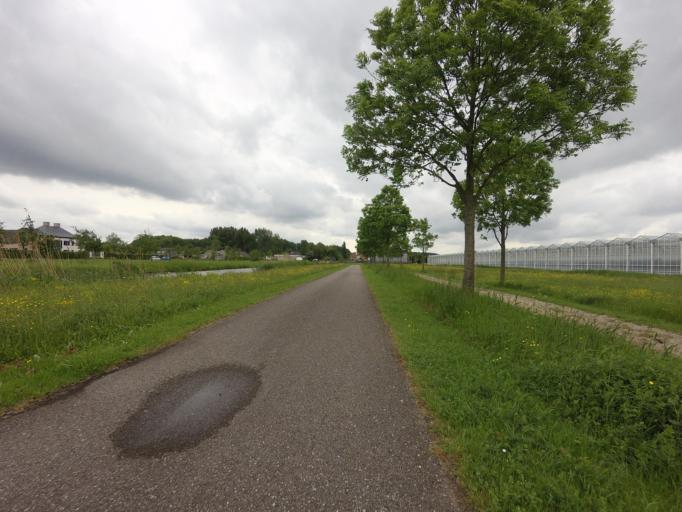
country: NL
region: South Holland
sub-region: Gemeente Lansingerland
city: Bergschenhoek
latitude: 51.9786
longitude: 4.5281
